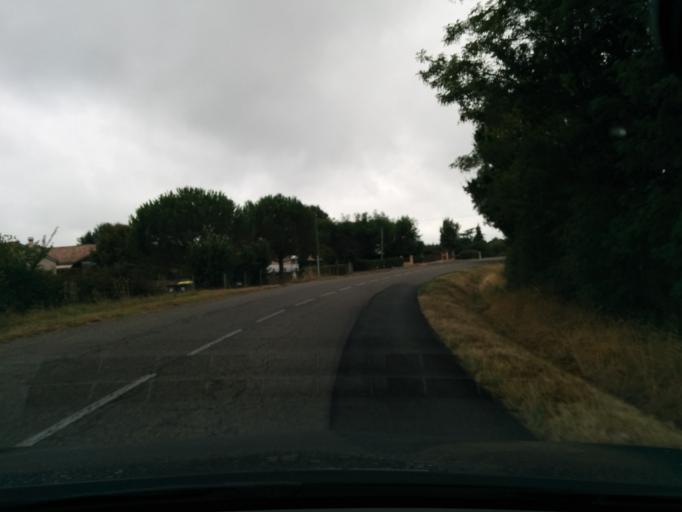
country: FR
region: Midi-Pyrenees
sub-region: Departement du Tarn-et-Garonne
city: Moissac
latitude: 44.1197
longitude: 1.0726
